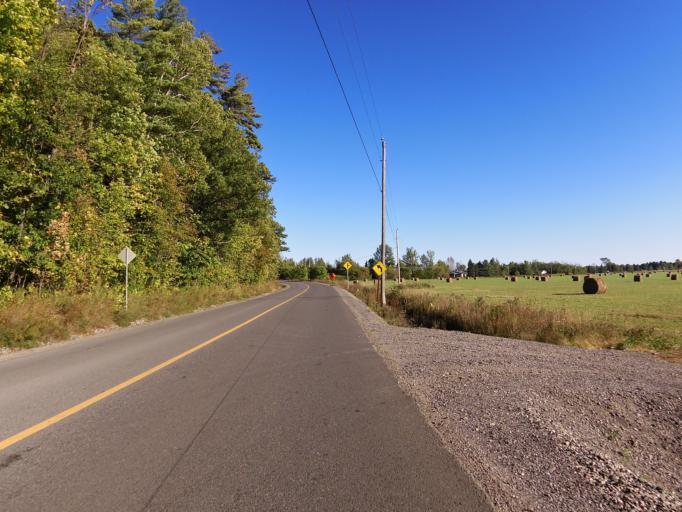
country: CA
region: Quebec
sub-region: Outaouais
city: Wakefield
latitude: 45.4960
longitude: -75.9133
